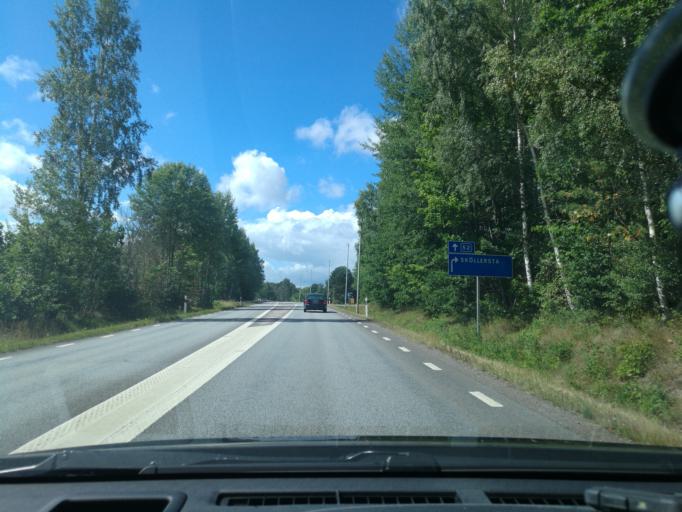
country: SE
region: OErebro
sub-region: Hallsbergs Kommun
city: Skollersta
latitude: 59.1334
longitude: 15.3365
